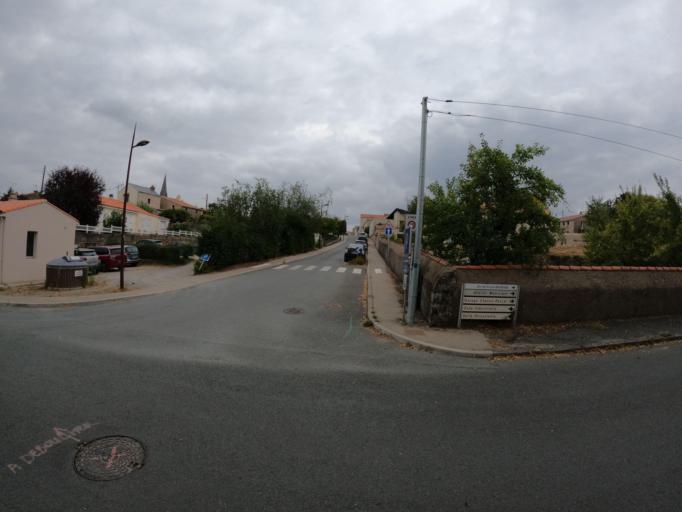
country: FR
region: Pays de la Loire
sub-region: Departement de la Vendee
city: Tiffauges
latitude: 47.0123
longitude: -1.1152
